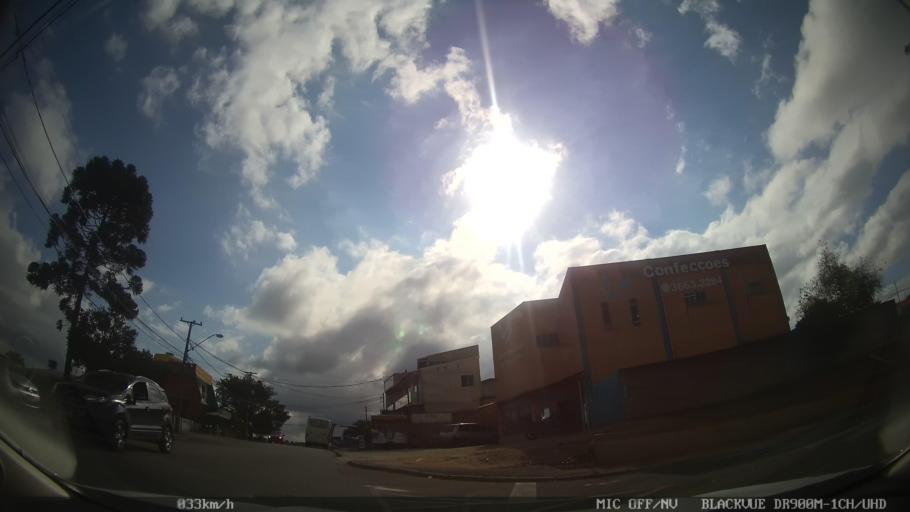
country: BR
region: Parana
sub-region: Colombo
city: Colombo
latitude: -25.3583
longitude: -49.1910
